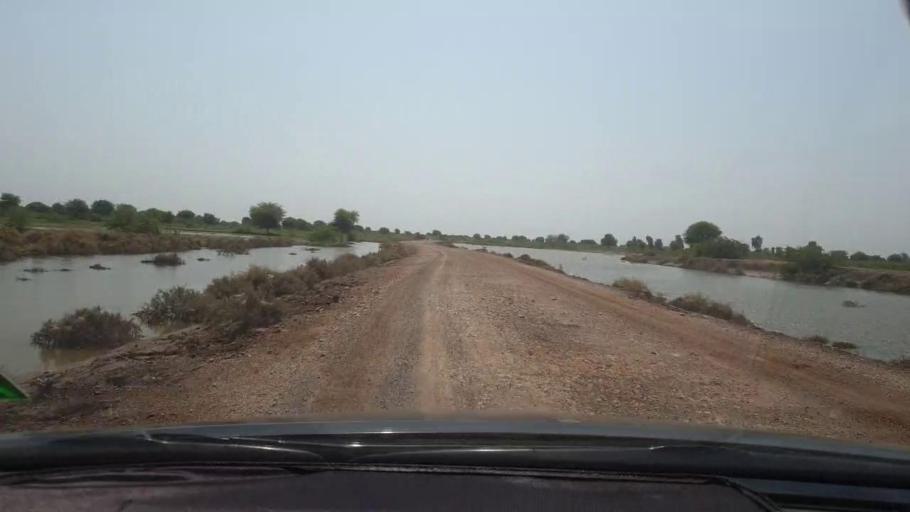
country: PK
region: Sindh
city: Tando Bago
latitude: 24.8100
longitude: 69.1657
